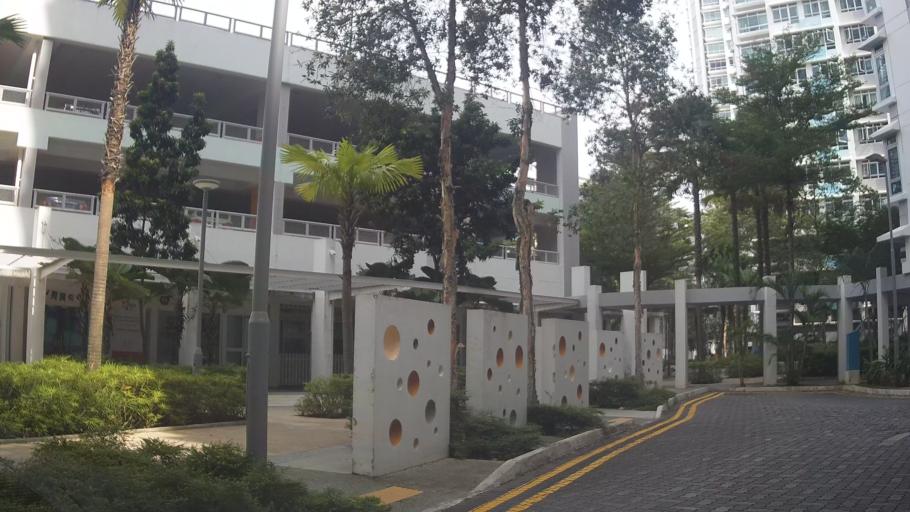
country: SG
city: Singapore
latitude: 1.3202
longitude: 103.8665
